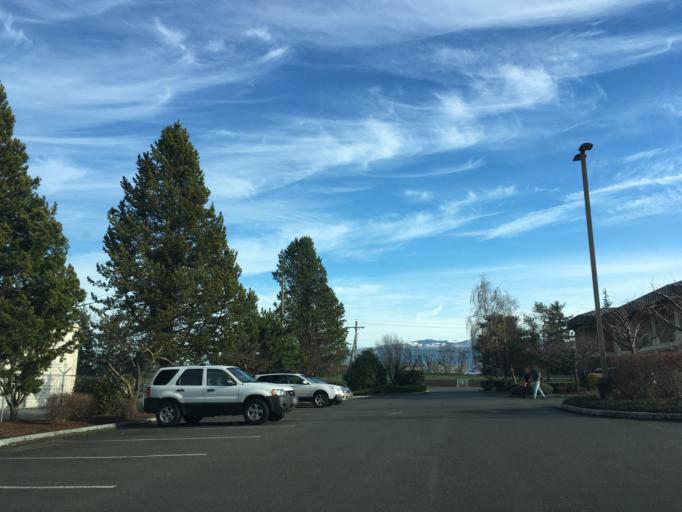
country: US
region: Washington
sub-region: Skagit County
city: Mount Vernon
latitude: 48.4339
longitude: -122.3433
